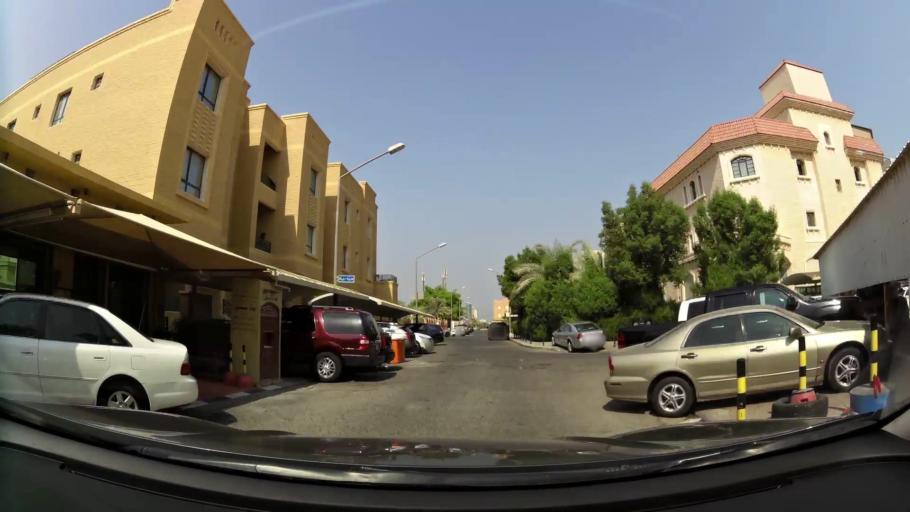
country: KW
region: Al Asimah
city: Ad Dasmah
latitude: 29.3526
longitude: 48.0114
